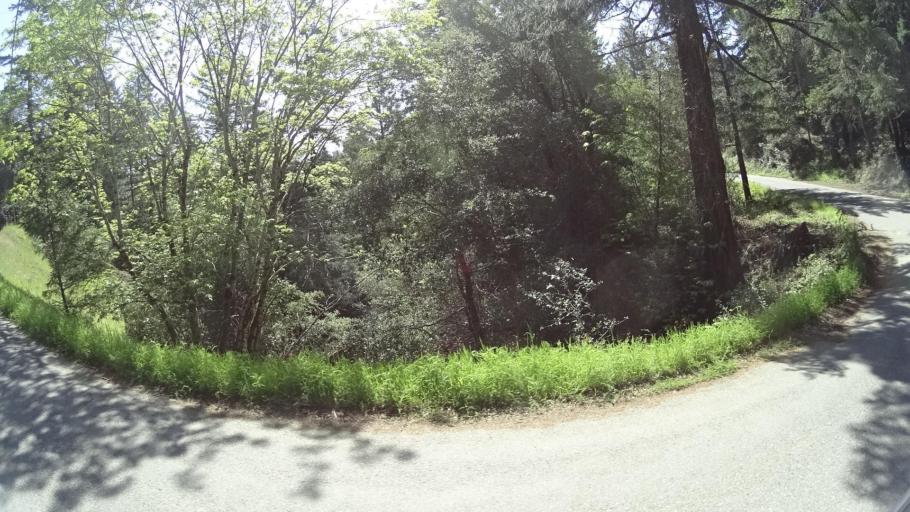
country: US
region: California
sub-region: Humboldt County
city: Redway
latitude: 40.0692
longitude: -123.6508
